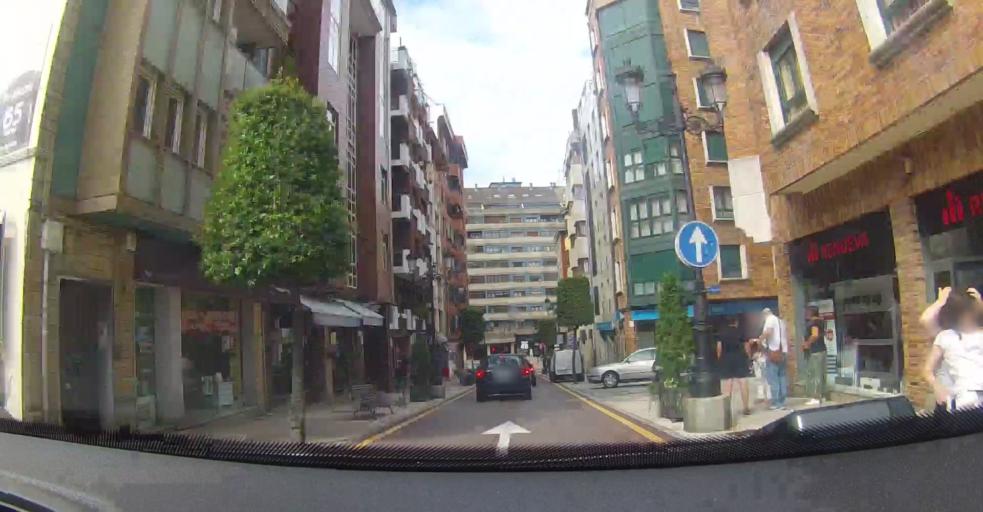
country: ES
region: Asturias
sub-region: Province of Asturias
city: Oviedo
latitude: 43.3662
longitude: -5.8475
